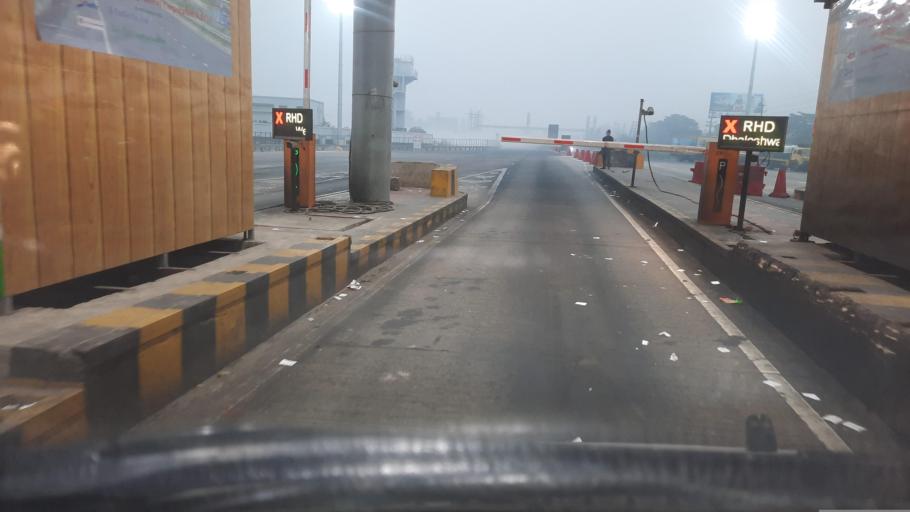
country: BD
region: Dhaka
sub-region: Dhaka
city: Dhaka
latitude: 23.6493
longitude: 90.3501
